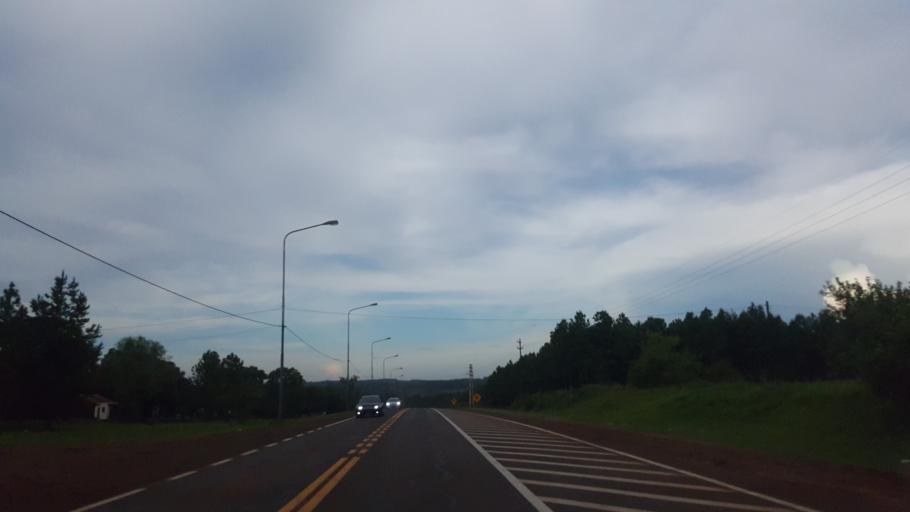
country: AR
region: Misiones
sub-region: Departamento de San Ignacio
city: San Ignacio
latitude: -27.2578
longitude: -55.5281
